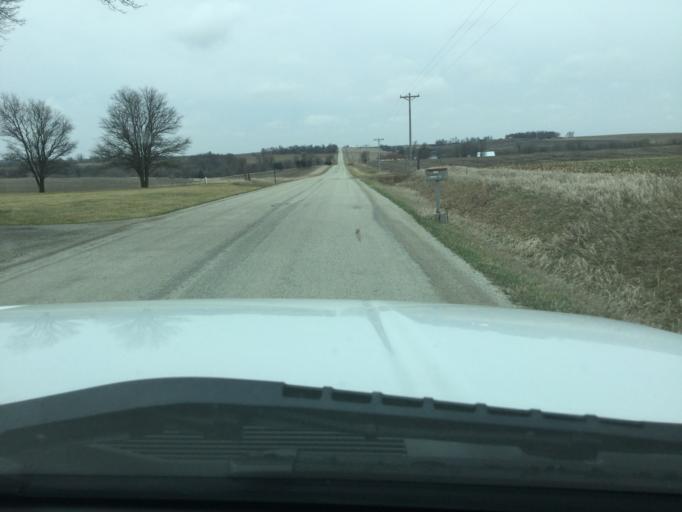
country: US
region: Kansas
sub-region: Nemaha County
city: Sabetha
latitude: 39.8856
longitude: -95.7140
